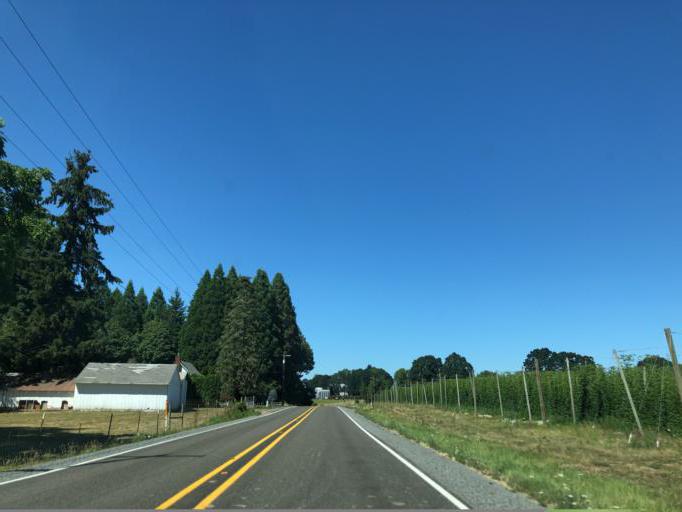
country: US
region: Oregon
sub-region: Marion County
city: Silverton
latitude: 45.0285
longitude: -122.7642
